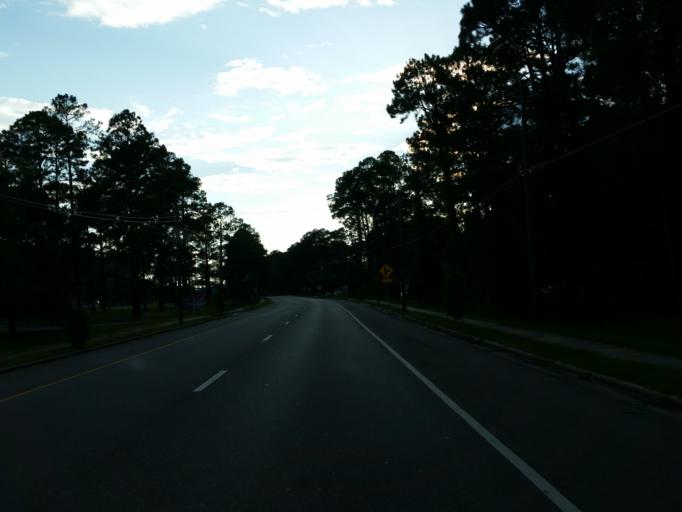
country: US
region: Georgia
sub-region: Clinch County
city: Homerville
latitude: 31.0358
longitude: -82.7530
